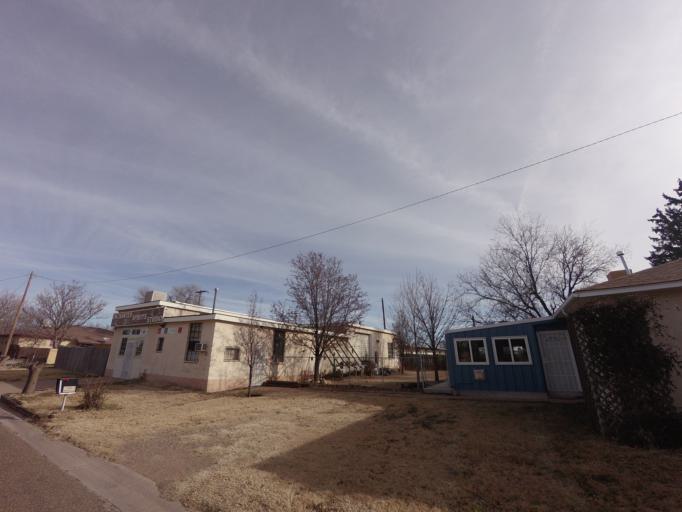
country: US
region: New Mexico
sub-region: Curry County
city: Clovis
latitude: 34.4124
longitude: -103.2174
